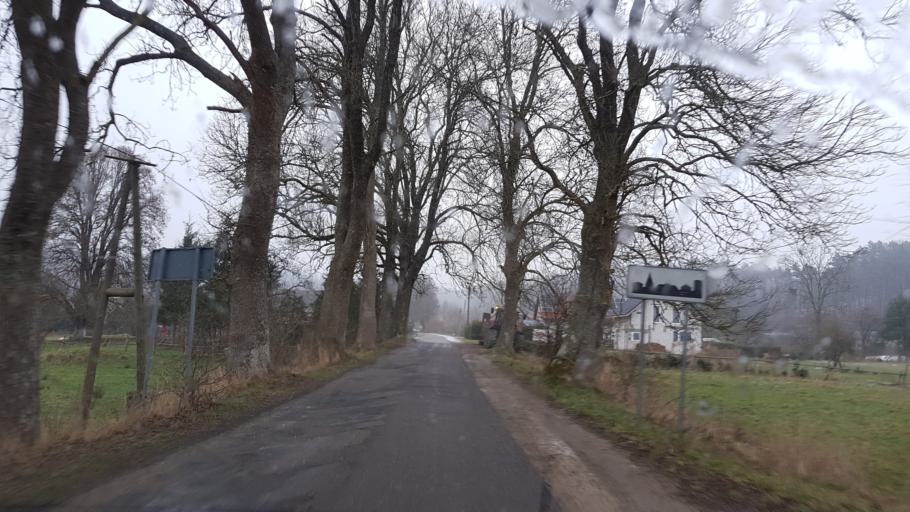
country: PL
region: West Pomeranian Voivodeship
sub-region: Powiat slawienski
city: Slawno
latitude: 54.2678
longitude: 16.5920
